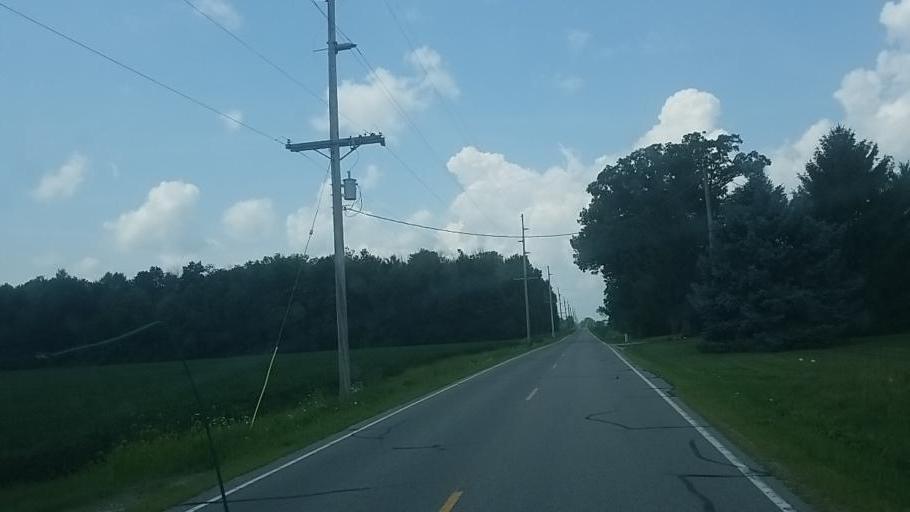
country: US
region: Ohio
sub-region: Crawford County
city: Bucyrus
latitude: 40.7980
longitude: -82.9429
